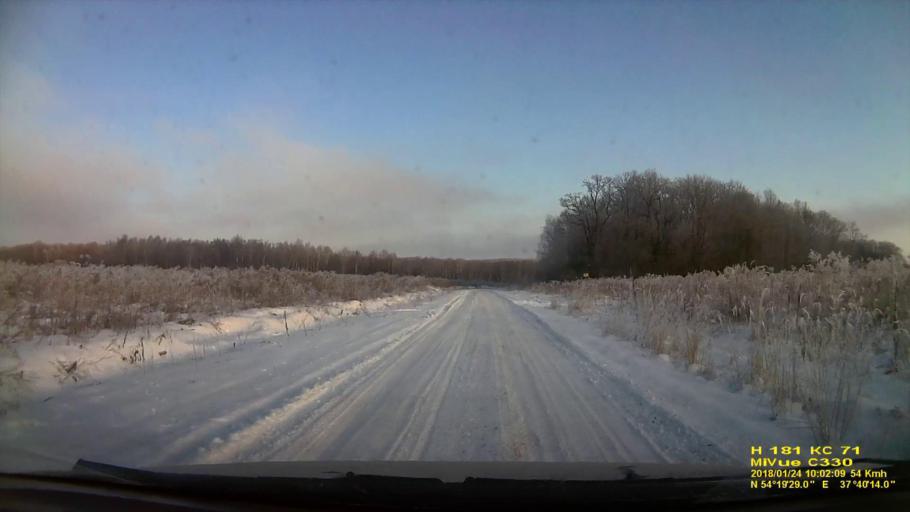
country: RU
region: Tula
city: Revyakino
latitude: 54.3249
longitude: 37.6706
